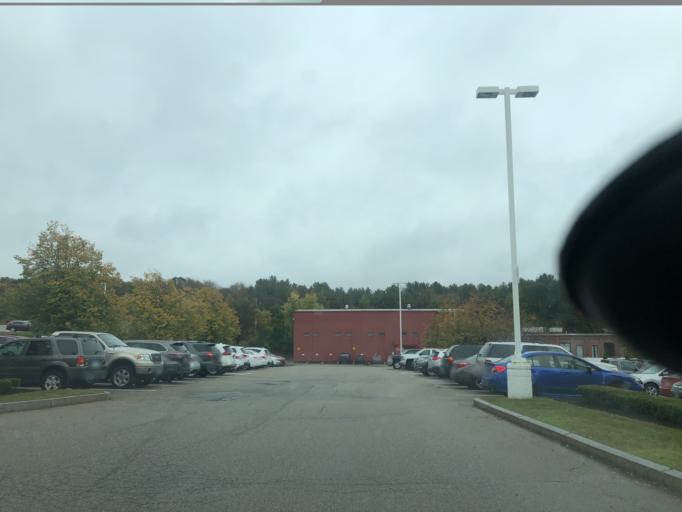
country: US
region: New Hampshire
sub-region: Strafford County
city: Dover
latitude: 43.2068
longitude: -70.8672
